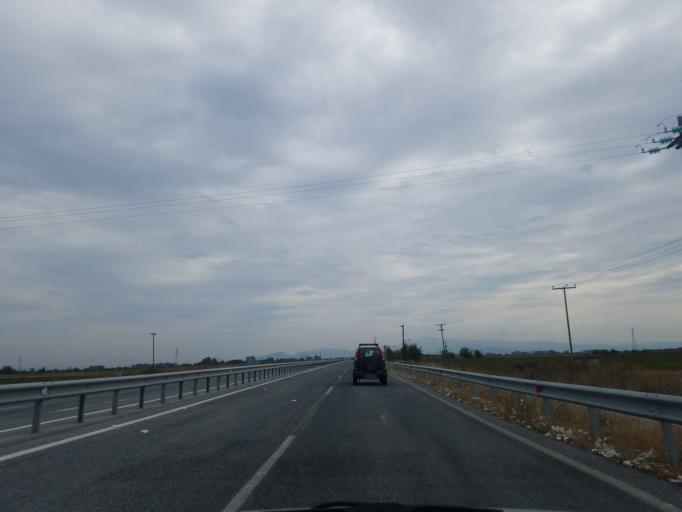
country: GR
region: Thessaly
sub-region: Nomos Kardhitsas
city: Sofades
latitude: 39.2999
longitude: 22.1379
